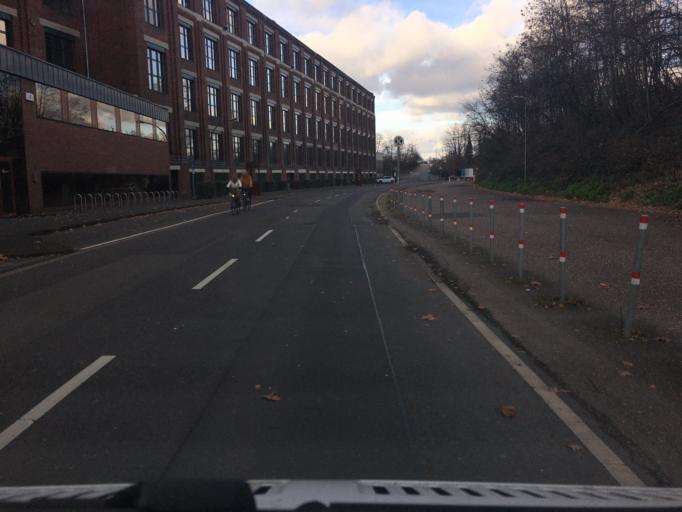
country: DE
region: North Rhine-Westphalia
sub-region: Regierungsbezirk Koln
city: Muelheim
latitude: 50.9706
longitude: 7.0184
